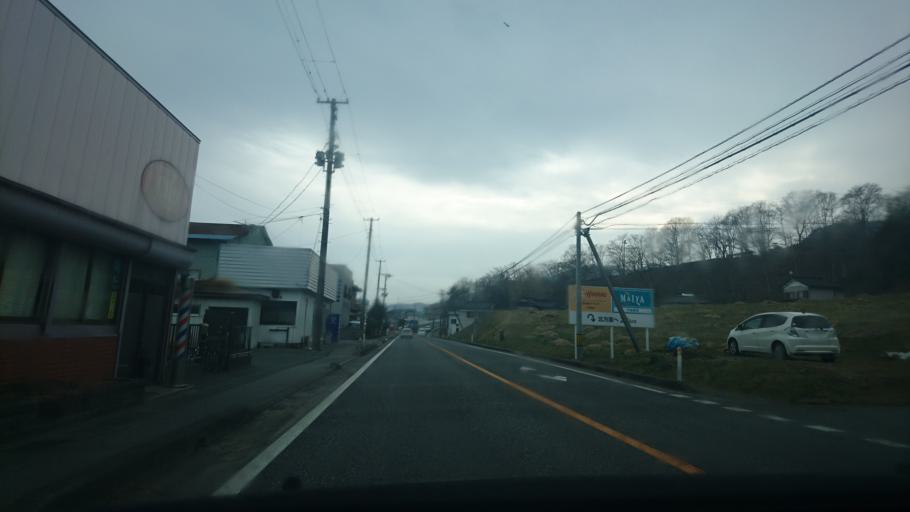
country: JP
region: Iwate
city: Ofunato
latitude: 39.0382
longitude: 141.7198
